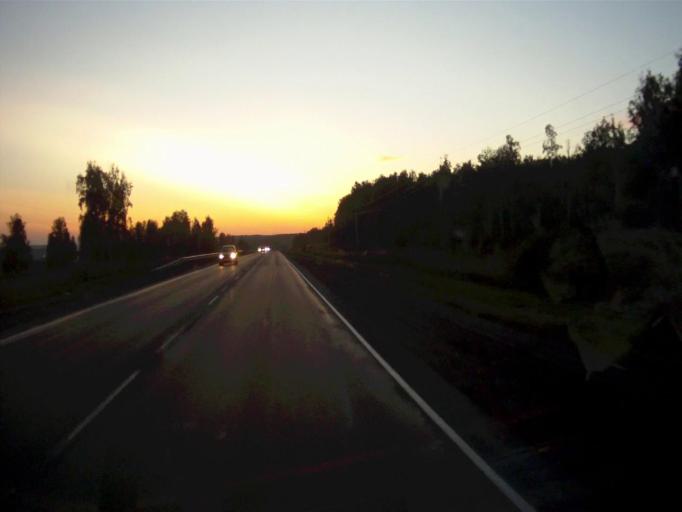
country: RU
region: Chelyabinsk
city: Poletayevo
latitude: 55.2218
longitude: 61.0170
